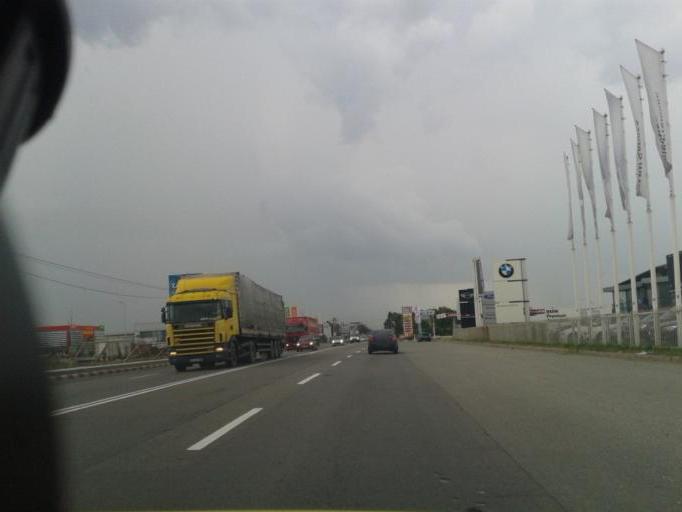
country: RO
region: Prahova
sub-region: Comuna Bucov
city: Bucov
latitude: 44.9603
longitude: 26.0567
